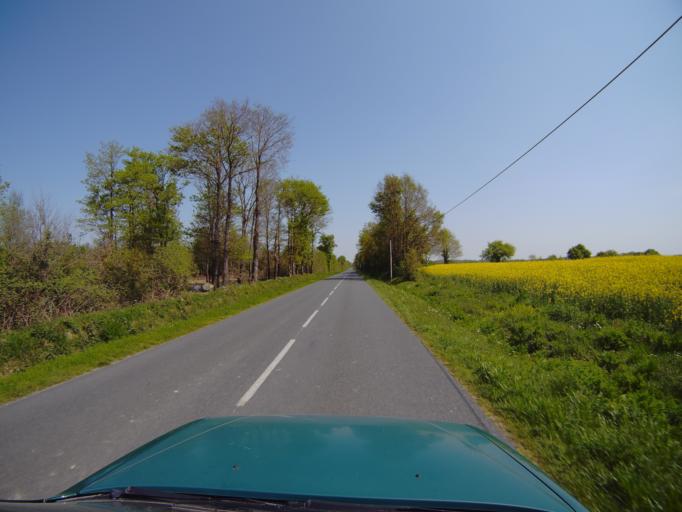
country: FR
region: Pays de la Loire
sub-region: Departement de la Vendee
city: Saint-Andre-Treize-Voies
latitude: 46.9393
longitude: -1.3940
